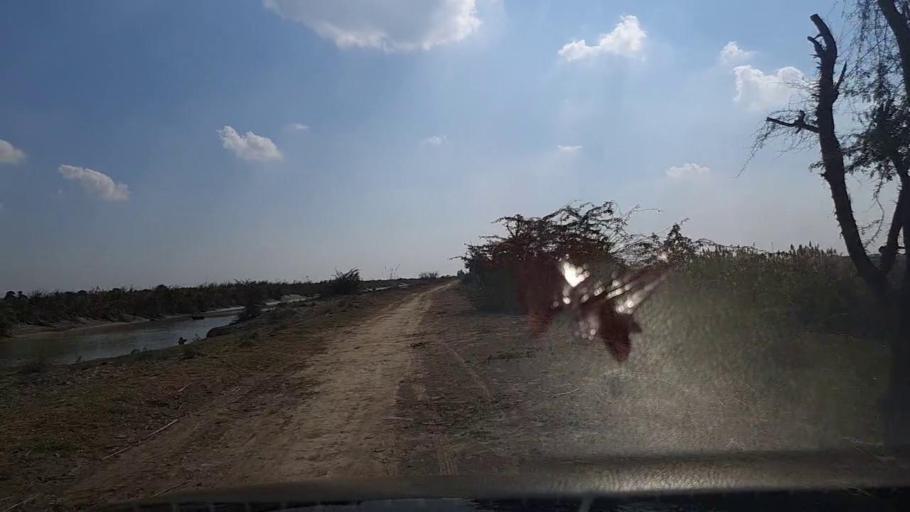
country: PK
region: Sindh
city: Tando Mittha Khan
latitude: 25.8452
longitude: 69.0743
